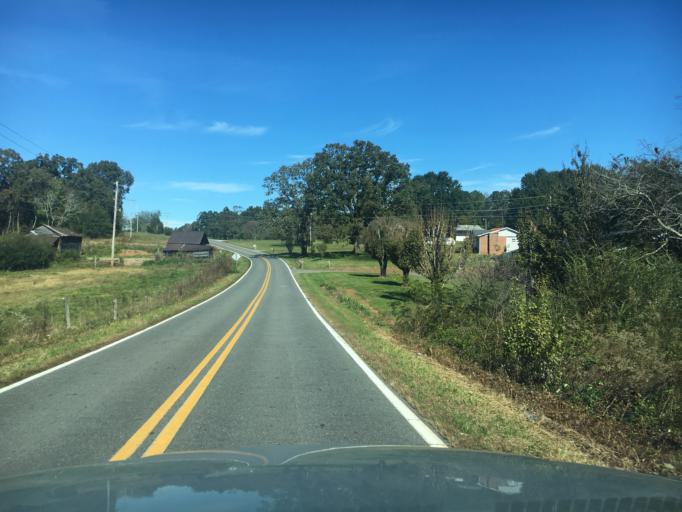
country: US
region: North Carolina
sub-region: Burke County
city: Salem
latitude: 35.6874
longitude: -81.7328
